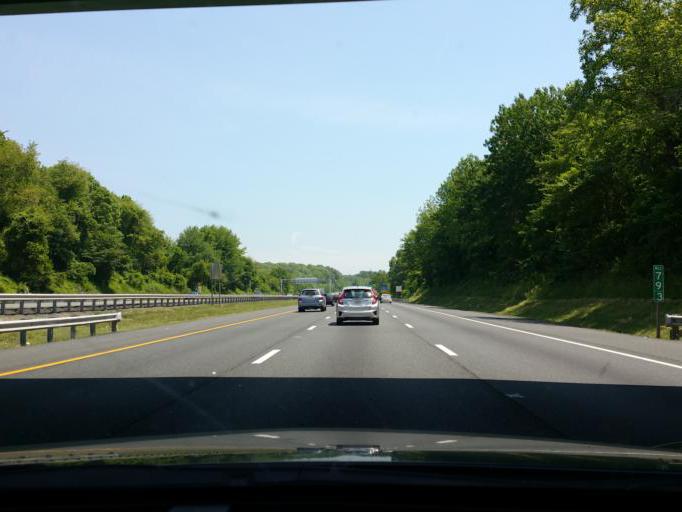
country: US
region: Maryland
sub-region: Harford County
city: Riverside
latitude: 39.4781
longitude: -76.2667
